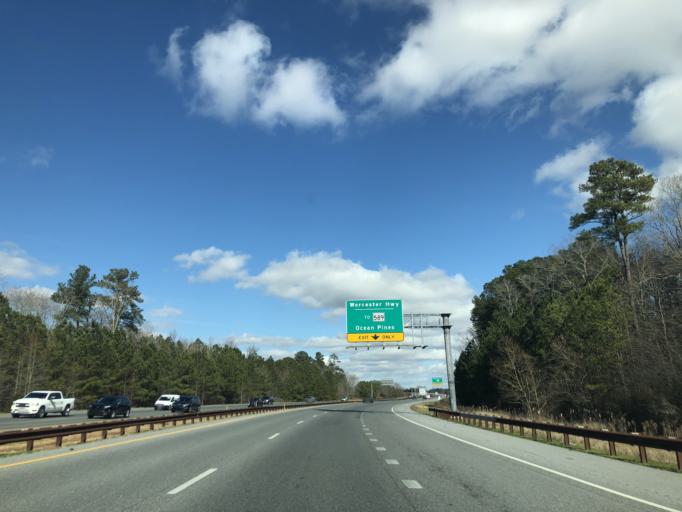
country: US
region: Maryland
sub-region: Worcester County
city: Ocean Pines
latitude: 38.3819
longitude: -75.2063
